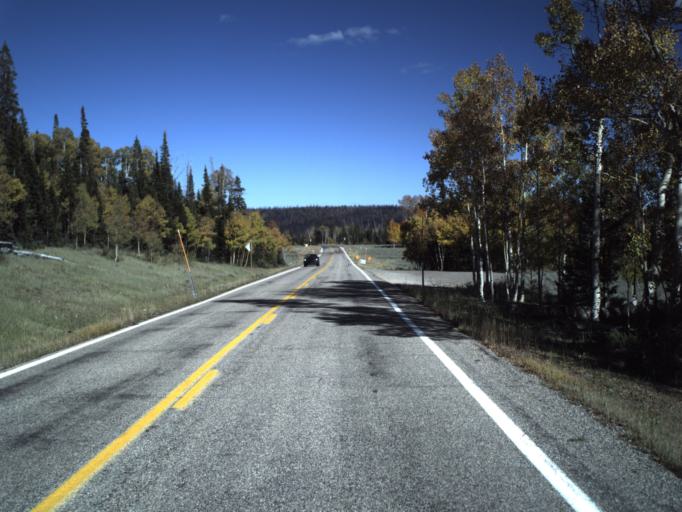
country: US
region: Utah
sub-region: Iron County
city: Parowan
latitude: 37.6585
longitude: -112.7480
